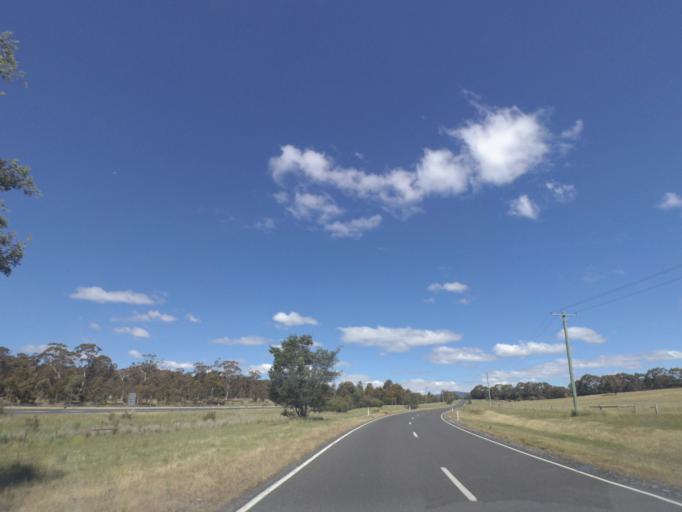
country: AU
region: Victoria
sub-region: Hume
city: Sunbury
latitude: -37.2978
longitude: 144.5053
